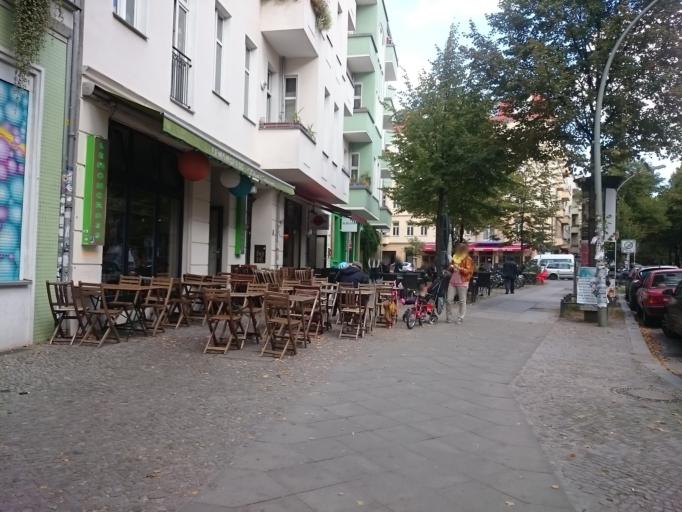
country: DE
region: Berlin
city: Friedrichshain Bezirk
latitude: 52.5123
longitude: 13.4574
